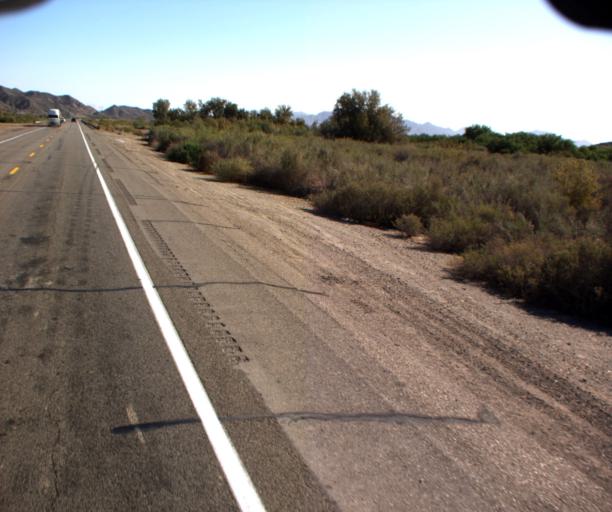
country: US
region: Arizona
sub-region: Yuma County
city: Fortuna Foothills
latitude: 32.7590
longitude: -114.4148
